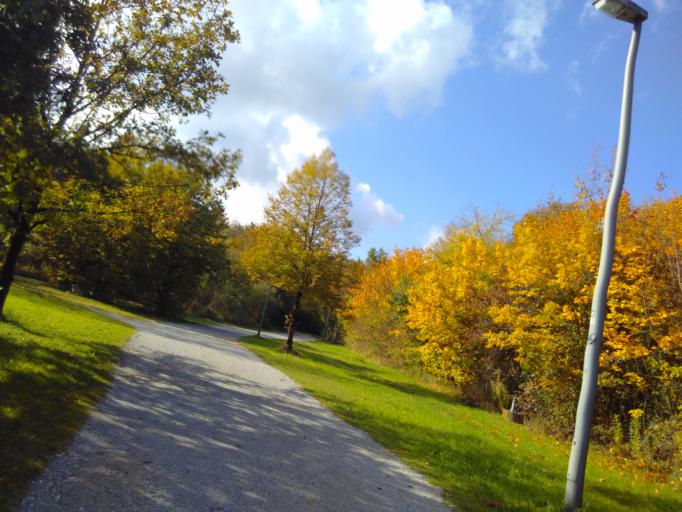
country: DE
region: Bavaria
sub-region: Upper Bavaria
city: Neuried
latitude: 48.1081
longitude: 11.4687
